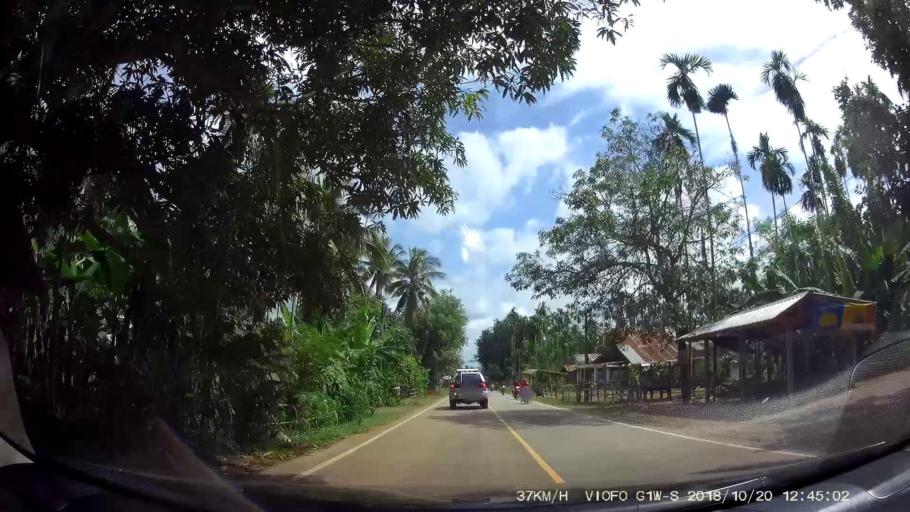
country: TH
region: Chaiyaphum
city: Khon San
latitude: 16.5371
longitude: 101.8727
